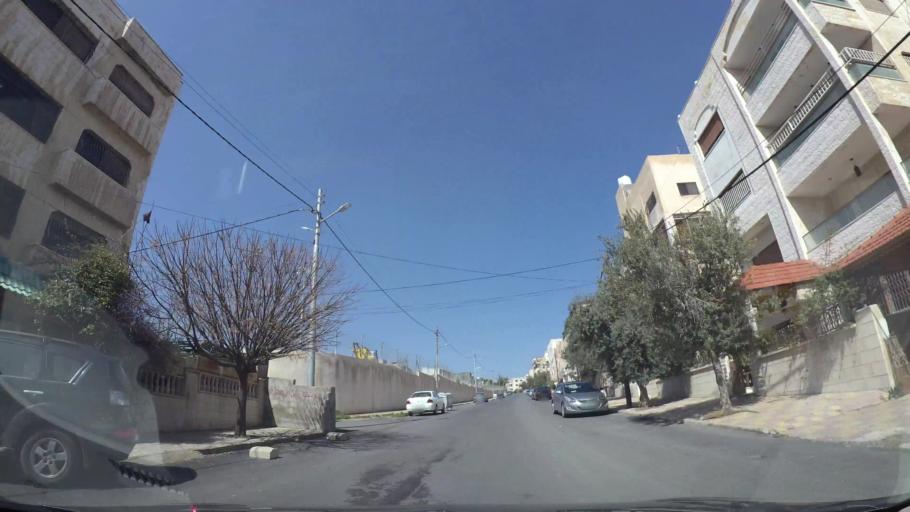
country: JO
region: Amman
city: Amman
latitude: 31.9750
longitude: 35.9872
